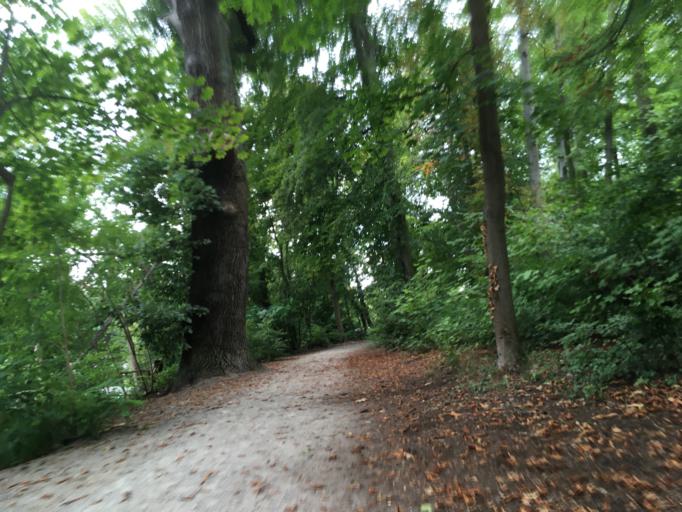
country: DE
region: Brandenburg
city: Kleinmachnow
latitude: 52.3977
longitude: 13.2173
